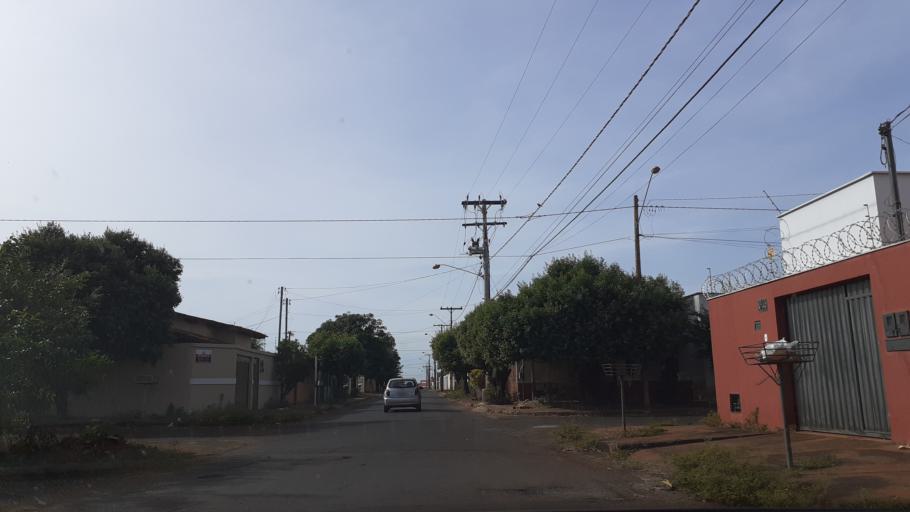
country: BR
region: Goias
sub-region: Itumbiara
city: Itumbiara
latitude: -18.4185
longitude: -49.2477
